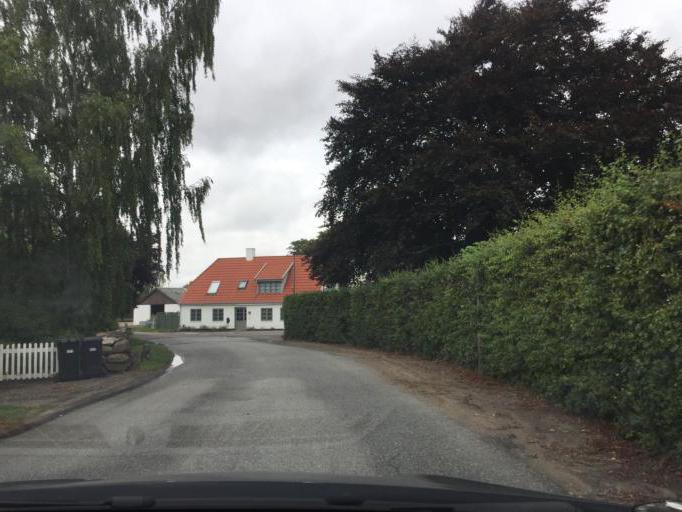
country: DK
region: South Denmark
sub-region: Assens Kommune
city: Harby
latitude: 55.2006
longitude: 10.1181
